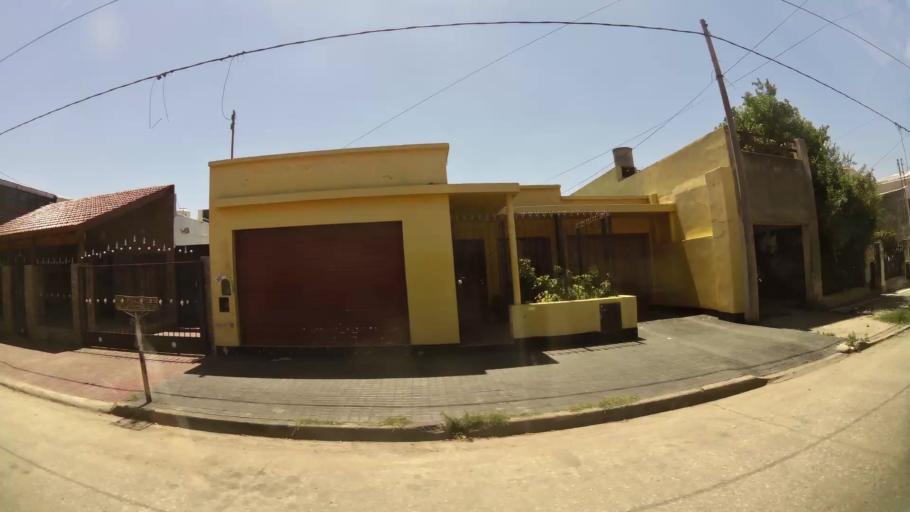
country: AR
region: Cordoba
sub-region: Departamento de Capital
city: Cordoba
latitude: -31.3868
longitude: -64.1494
